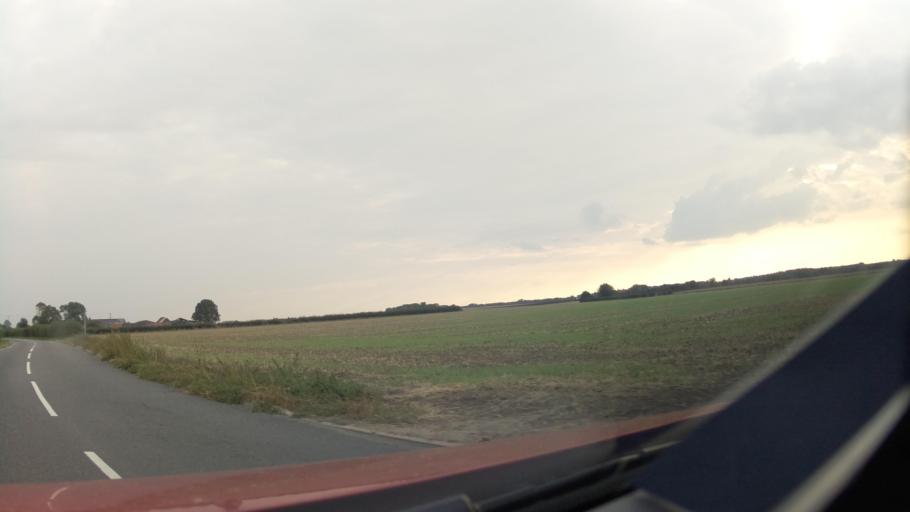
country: GB
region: England
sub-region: Lincolnshire
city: Skellingthorpe
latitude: 53.1376
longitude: -0.6450
